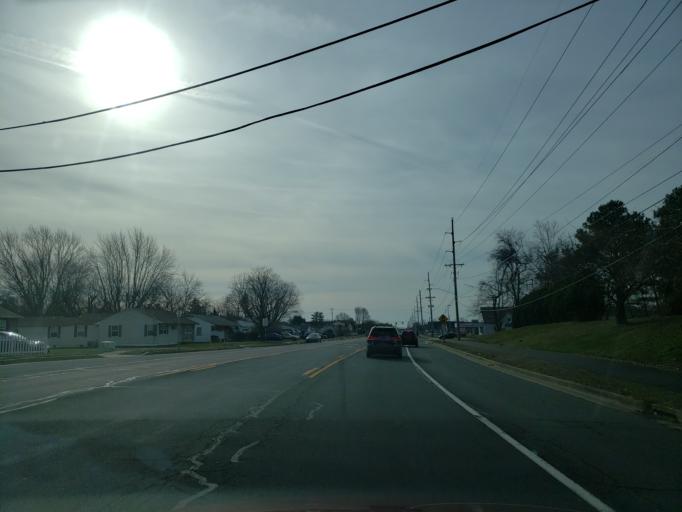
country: US
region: Delaware
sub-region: Kent County
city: Dover
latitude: 39.1716
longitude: -75.5474
